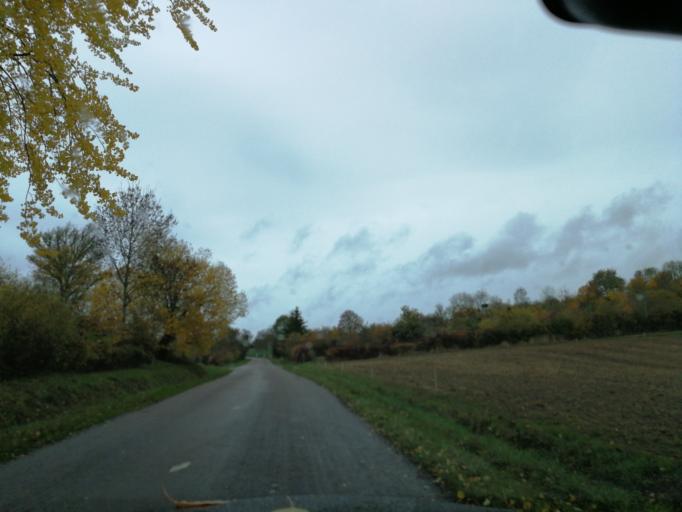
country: FR
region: Bourgogne
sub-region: Departement de la Cote-d'Or
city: Fleurey-sur-Ouche
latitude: 47.3286
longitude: 4.7877
